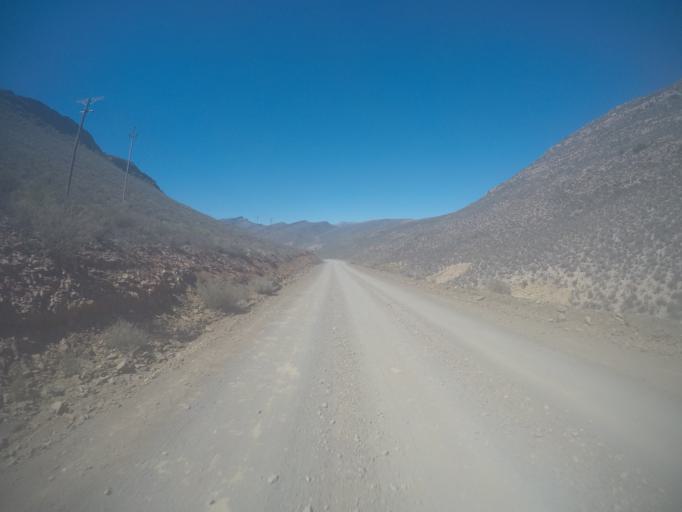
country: ZA
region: Western Cape
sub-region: West Coast District Municipality
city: Clanwilliam
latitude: -32.5375
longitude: 19.3559
